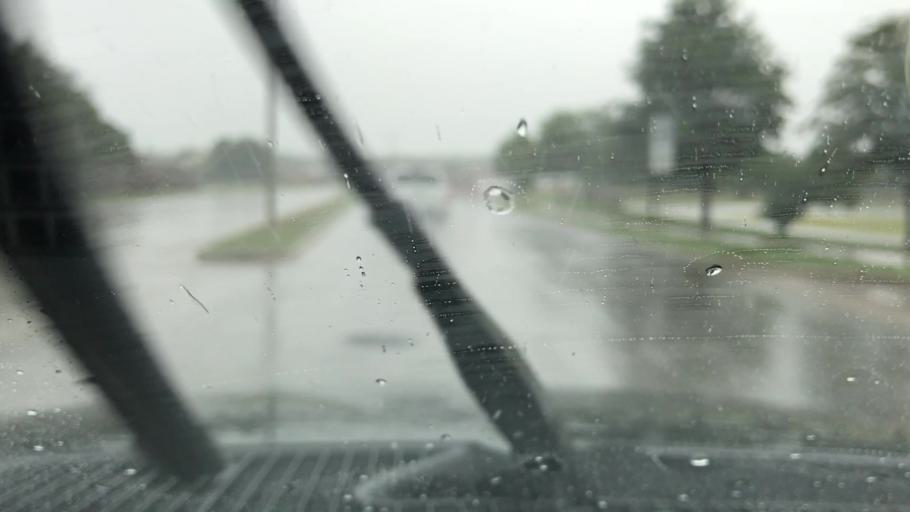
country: US
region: Texas
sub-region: Williamson County
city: Cedar Park
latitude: 30.5298
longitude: -97.8577
